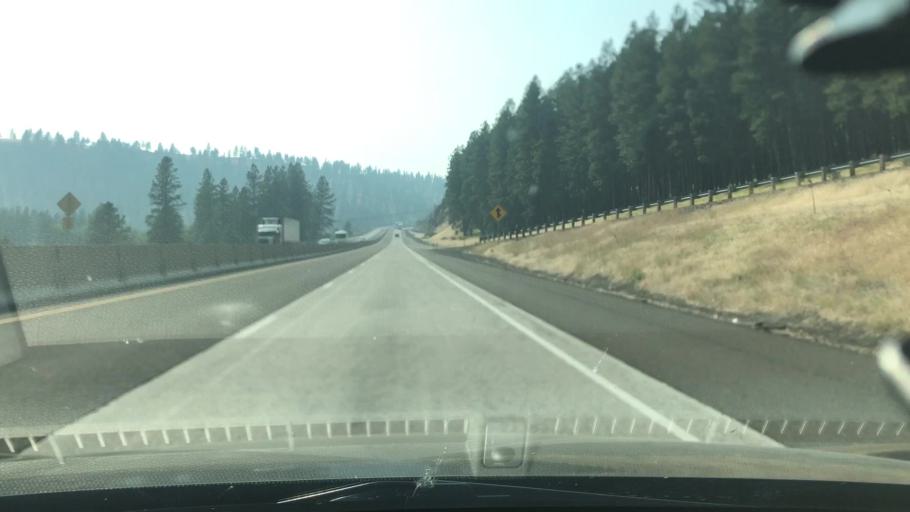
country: US
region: Oregon
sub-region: Union County
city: La Grande
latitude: 45.3425
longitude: -118.2319
